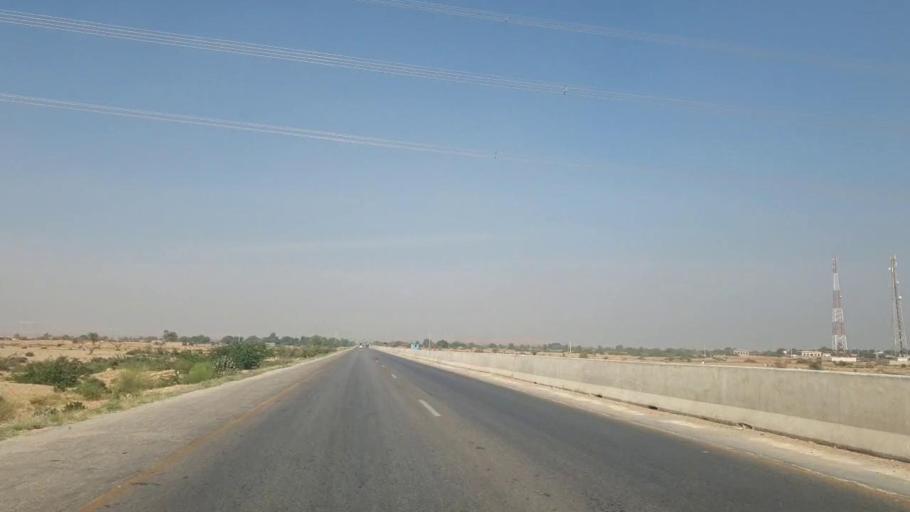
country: PK
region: Sindh
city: Matiari
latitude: 25.5882
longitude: 68.3104
